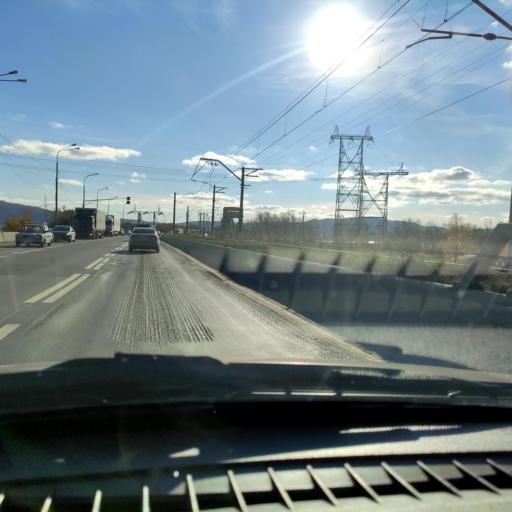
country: RU
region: Samara
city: Zhigulevsk
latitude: 53.4644
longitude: 49.5029
